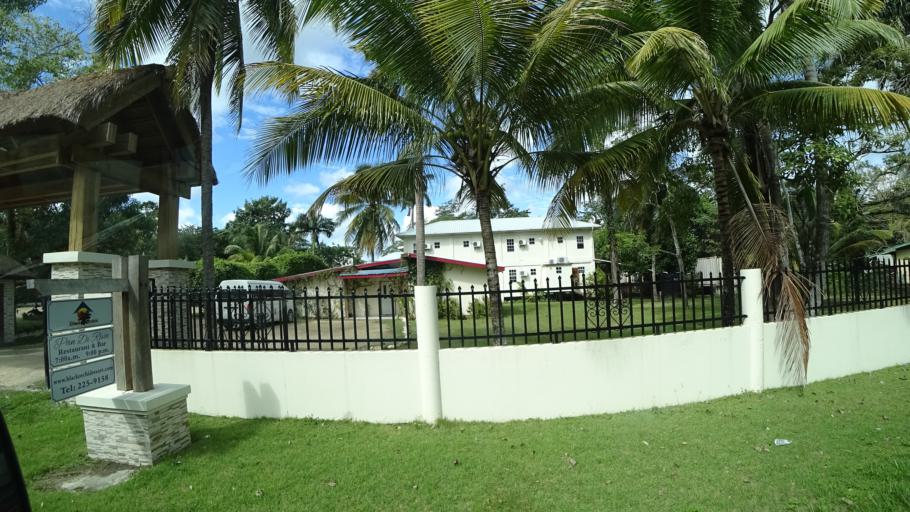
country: BZ
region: Belize
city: Belize City
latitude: 17.5704
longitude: -88.3957
